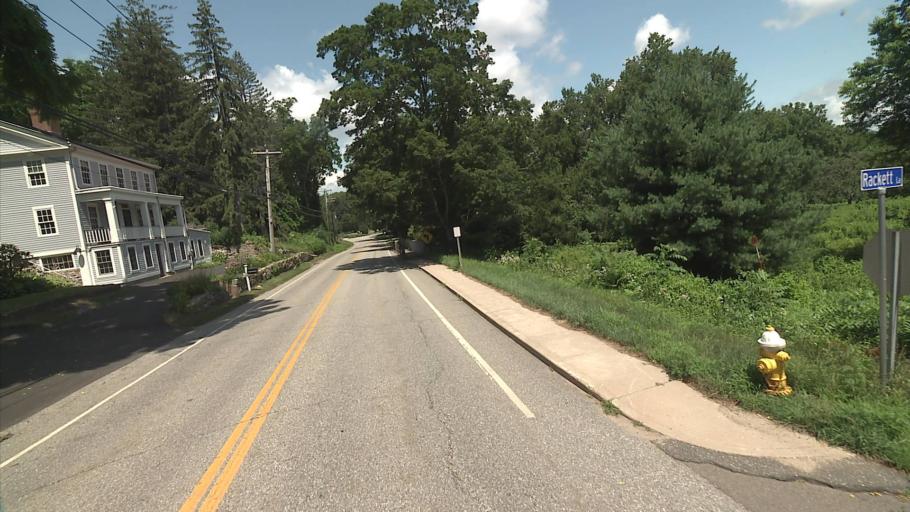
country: US
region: Connecticut
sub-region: Middlesex County
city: Essex Village
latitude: 41.3450
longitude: -72.3932
